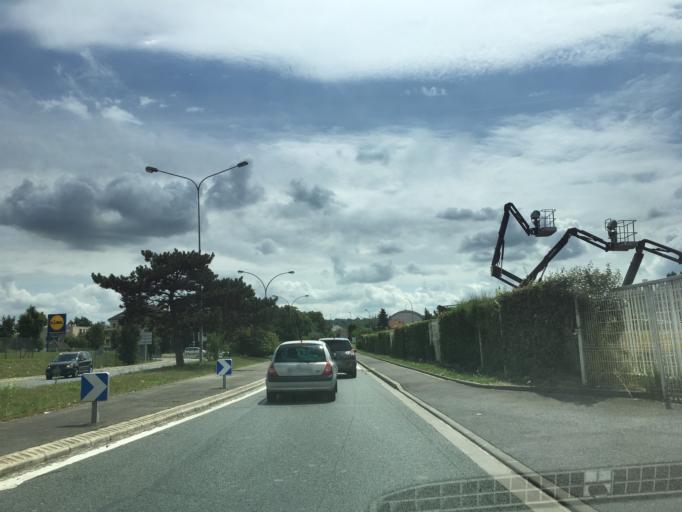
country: FR
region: Ile-de-France
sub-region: Departement du Val-de-Marne
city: Bonneuil-sur-Marne
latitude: 48.7578
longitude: 2.4821
